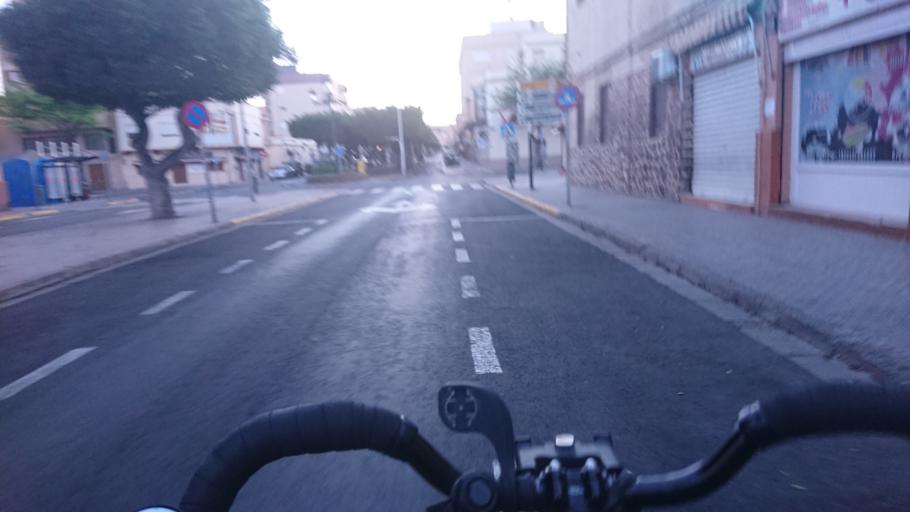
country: ES
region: Melilla
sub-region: Melilla
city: Melilla
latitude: 35.2774
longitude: -2.9391
